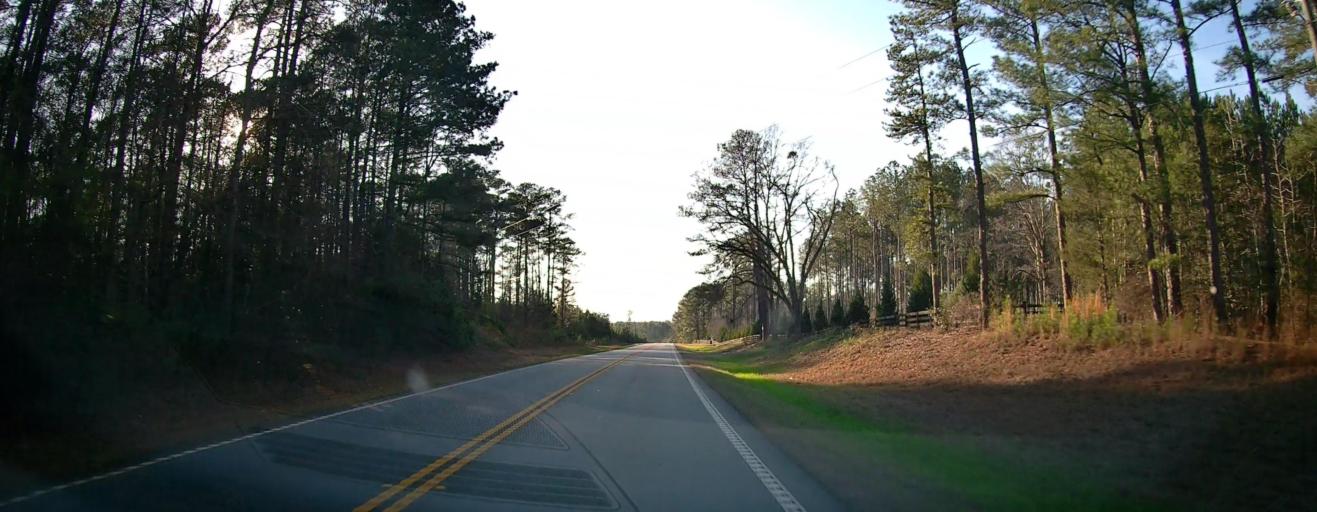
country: US
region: Alabama
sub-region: Chambers County
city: Valley
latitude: 32.7427
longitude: -85.0456
